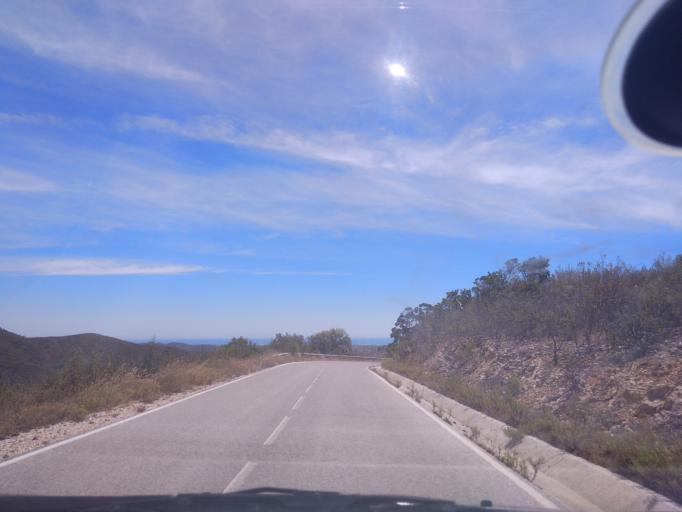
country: PT
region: Faro
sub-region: Sao Bras de Alportel
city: Sao Bras de Alportel
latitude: 37.1960
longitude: -7.8001
